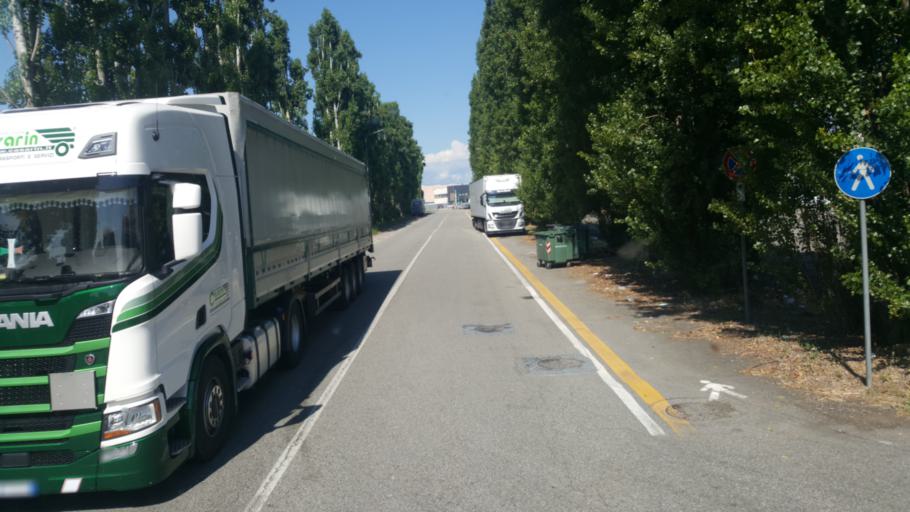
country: IT
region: Piedmont
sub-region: Provincia di Novara
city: Biandrate
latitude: 45.4627
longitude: 8.4632
